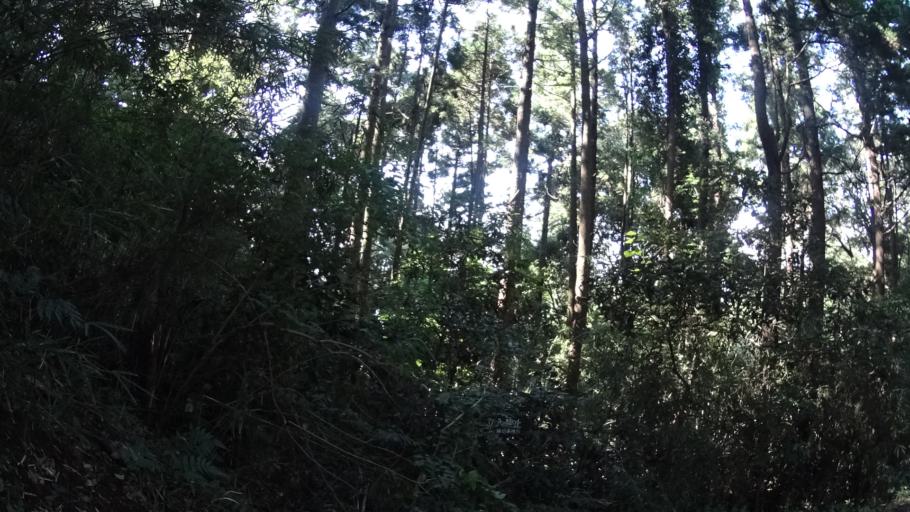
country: JP
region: Kanagawa
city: Kamakura
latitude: 35.3592
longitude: 139.5921
